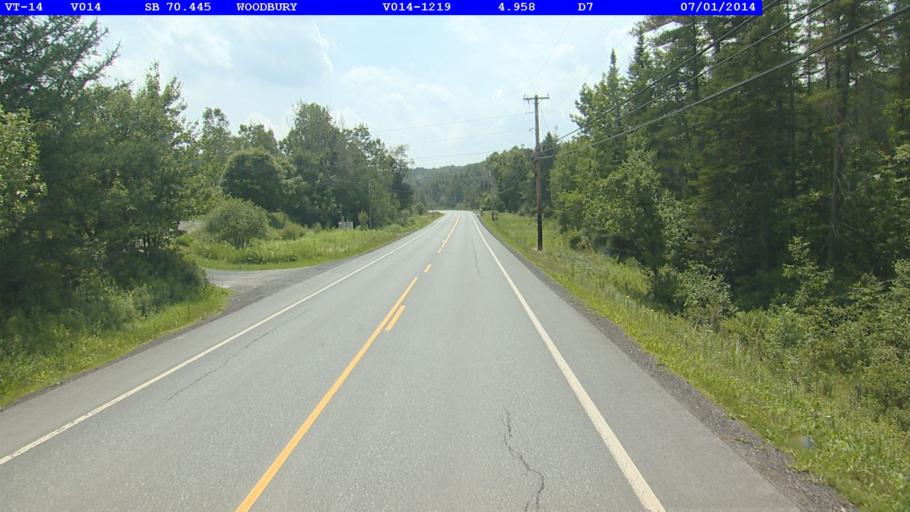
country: US
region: Vermont
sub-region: Caledonia County
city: Hardwick
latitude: 44.4587
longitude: -72.4190
